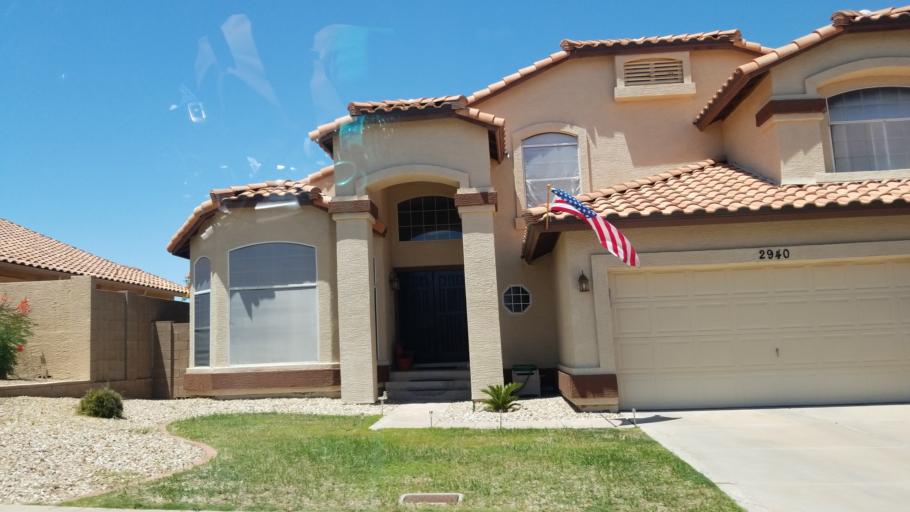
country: US
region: Arizona
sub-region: Maricopa County
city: Paradise Valley
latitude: 33.6128
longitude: -112.0188
